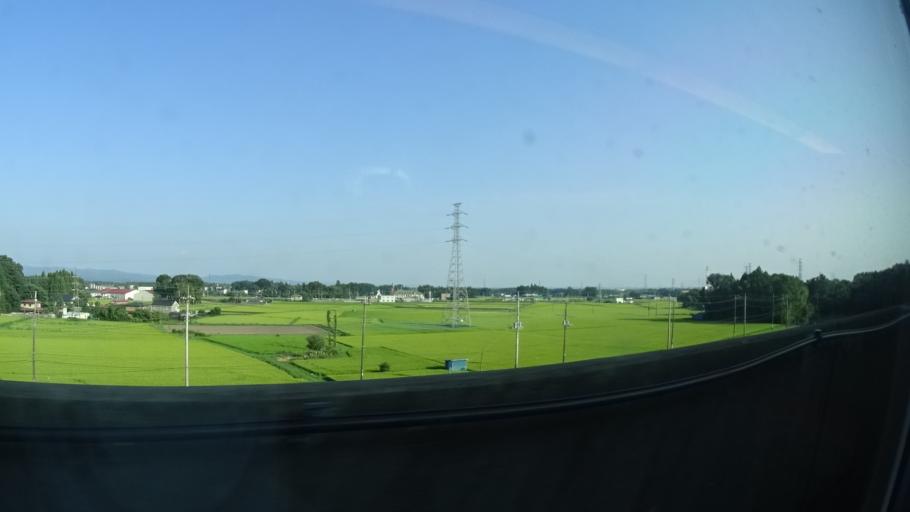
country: JP
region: Tochigi
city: Kuroiso
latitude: 36.9504
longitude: 140.0410
